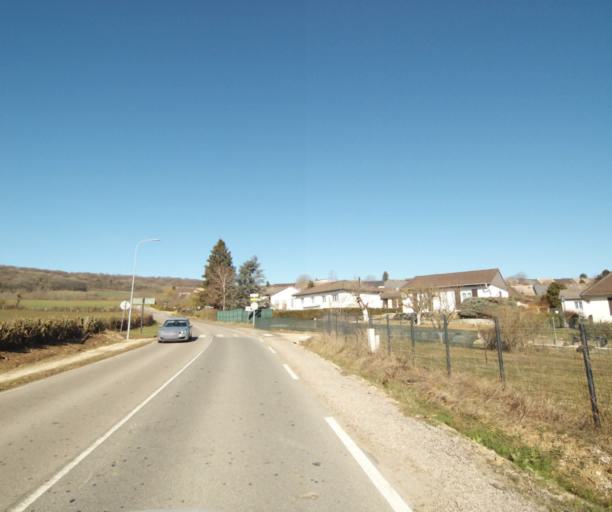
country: FR
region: Lorraine
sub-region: Departement de Meurthe-et-Moselle
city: Ludres
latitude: 48.6131
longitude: 6.1611
